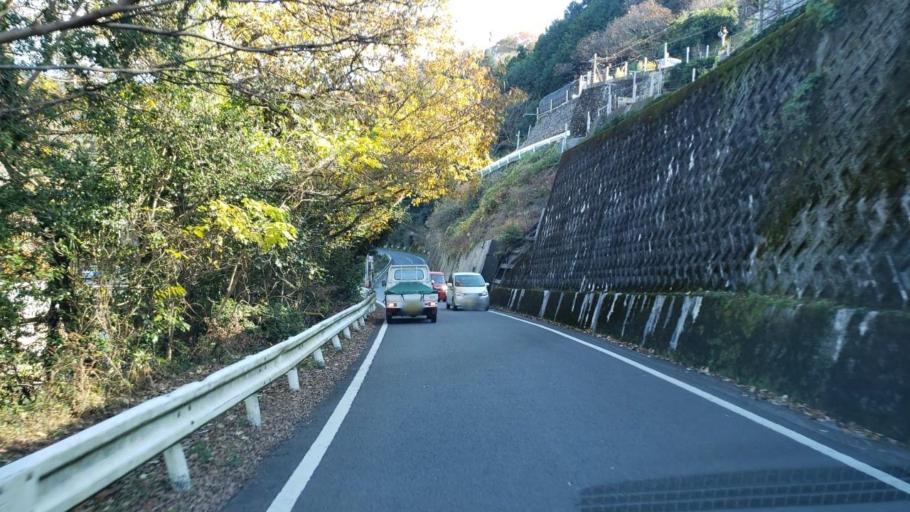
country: JP
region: Tokushima
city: Wakimachi
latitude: 34.0219
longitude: 134.0317
